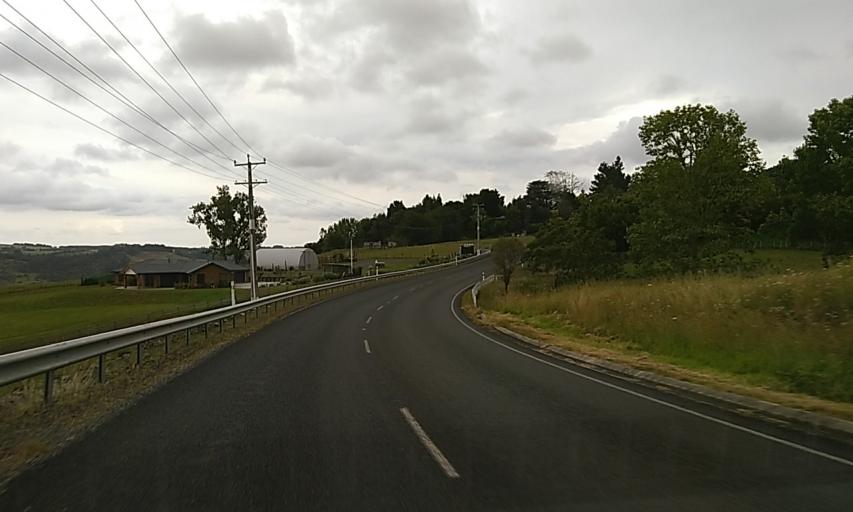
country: NZ
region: Auckland
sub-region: Auckland
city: Pukekohe East
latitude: -37.3111
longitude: 174.9380
